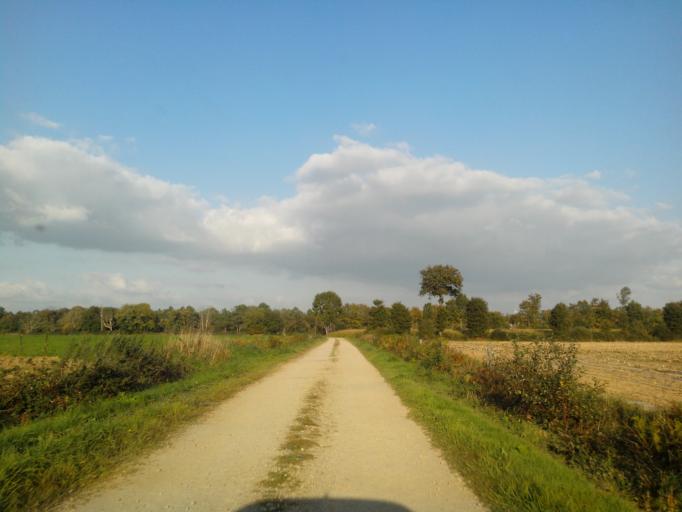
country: FR
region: Brittany
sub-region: Departement du Morbihan
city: Guilliers
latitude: 48.1189
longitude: -2.3790
